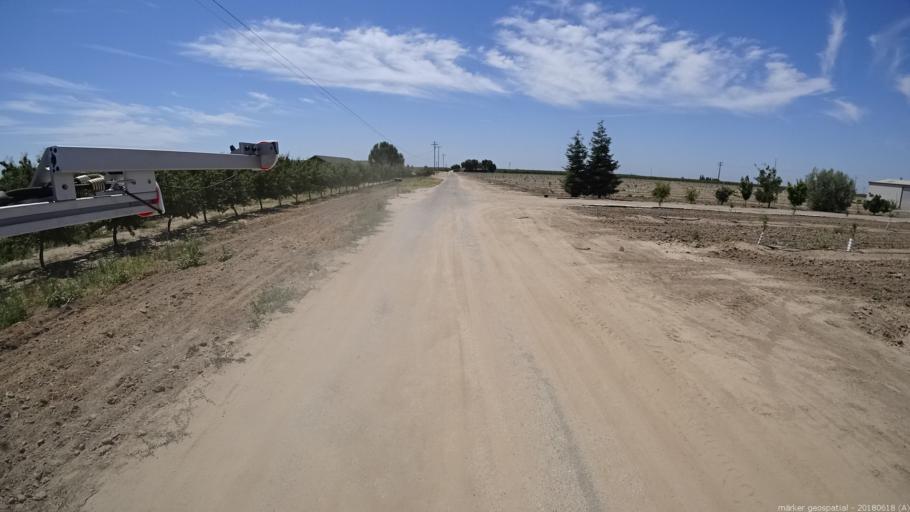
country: US
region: California
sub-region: Madera County
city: Parkwood
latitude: 36.8615
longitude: -120.1013
